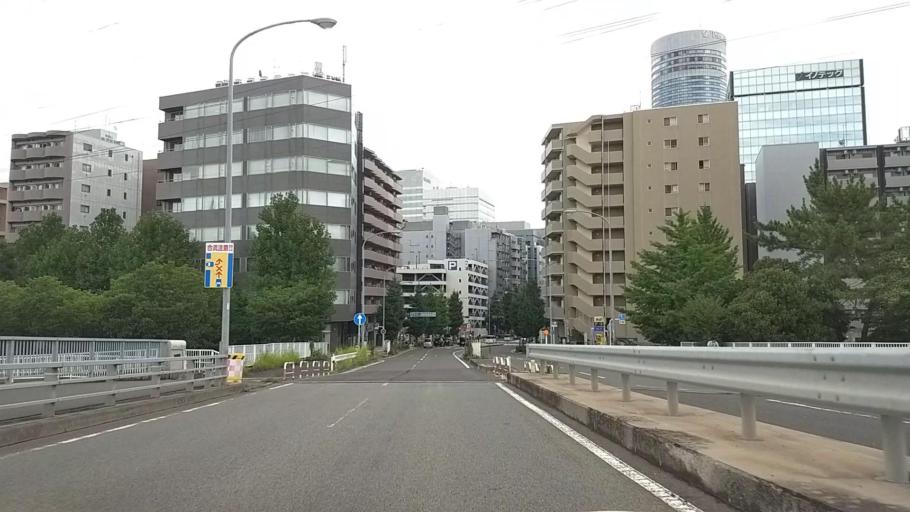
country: JP
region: Kanagawa
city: Yokohama
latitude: 35.5126
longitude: 139.6166
